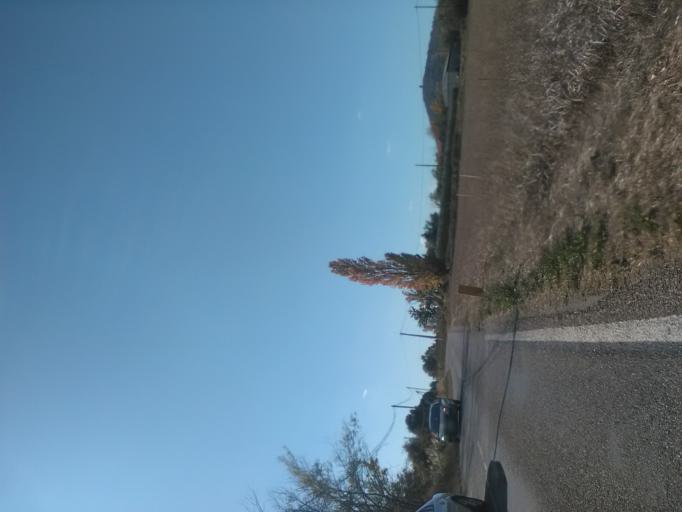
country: FR
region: Provence-Alpes-Cote d'Azur
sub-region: Departement des Alpes-de-Haute-Provence
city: Manosque
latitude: 43.8358
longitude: 5.8258
